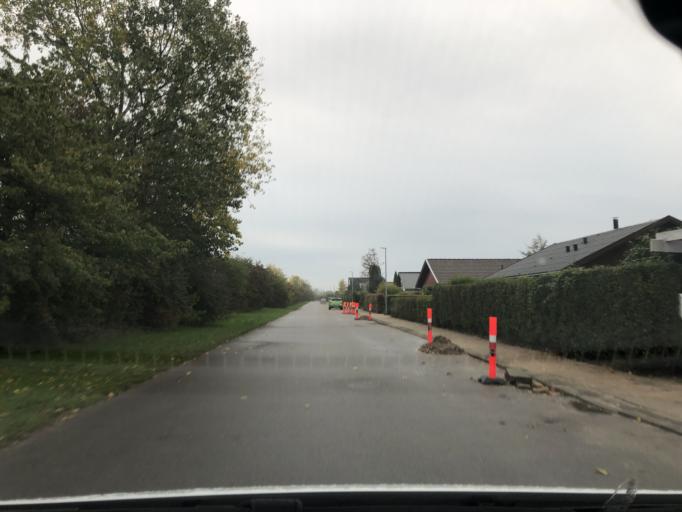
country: DK
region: Capital Region
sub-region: Tarnby Kommune
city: Tarnby
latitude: 55.5948
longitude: 12.5898
